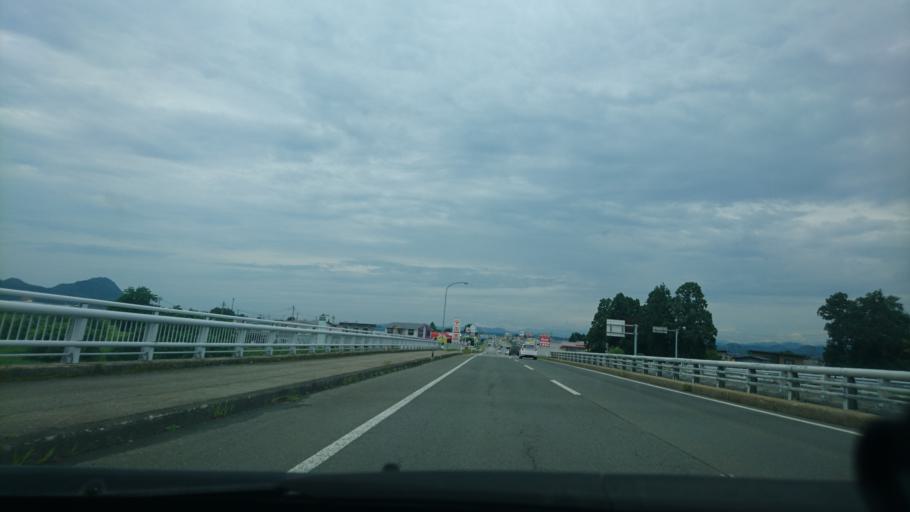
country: JP
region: Akita
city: Omagari
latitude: 39.4624
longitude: 140.4922
